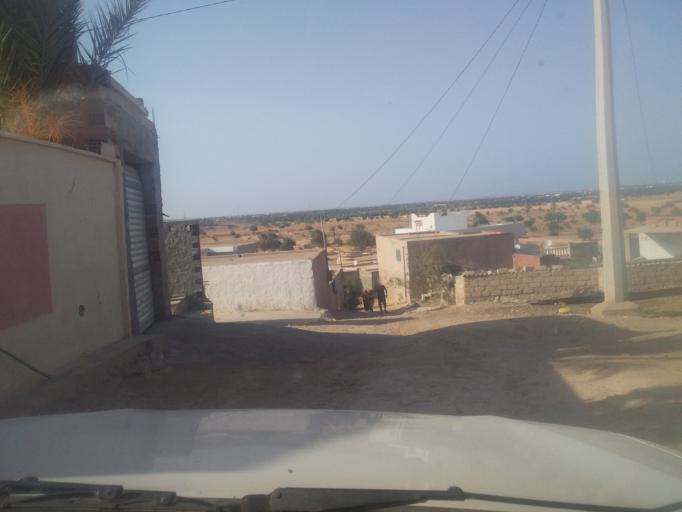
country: TN
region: Qabis
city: Matmata
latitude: 33.5829
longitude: 10.2554
